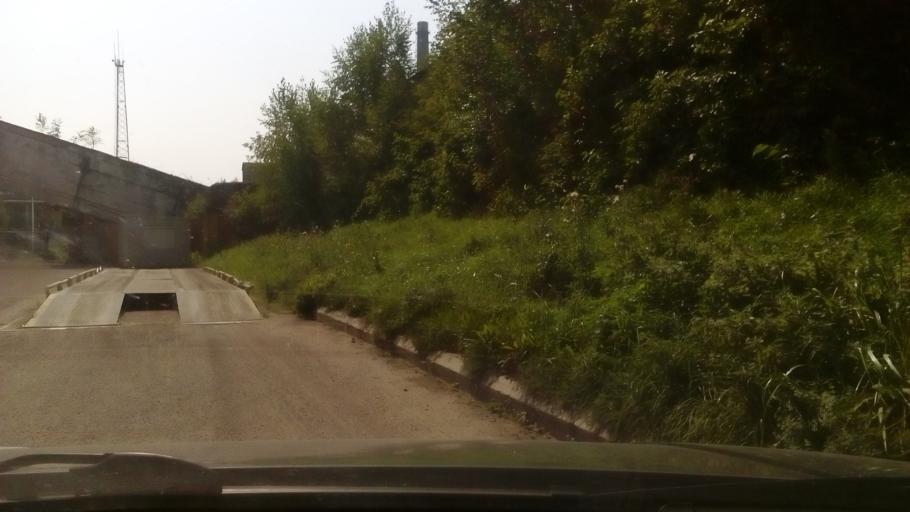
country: LT
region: Alytaus apskritis
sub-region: Alytus
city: Alytus
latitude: 54.4261
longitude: 24.0131
